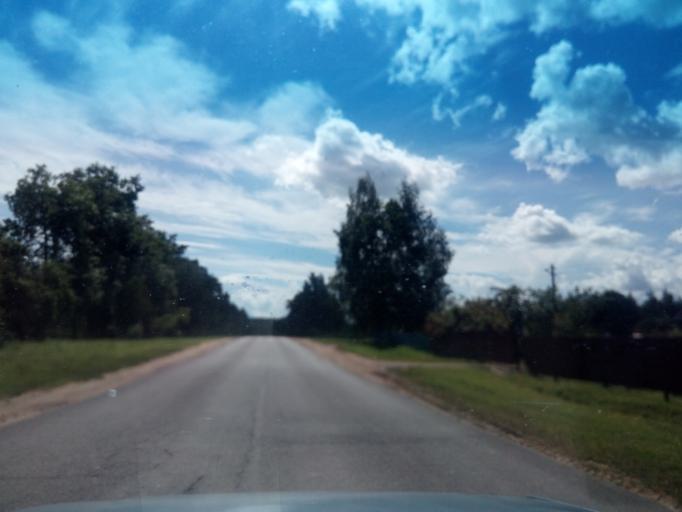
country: BY
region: Vitebsk
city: Dzisna
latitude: 55.6590
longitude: 28.3237
